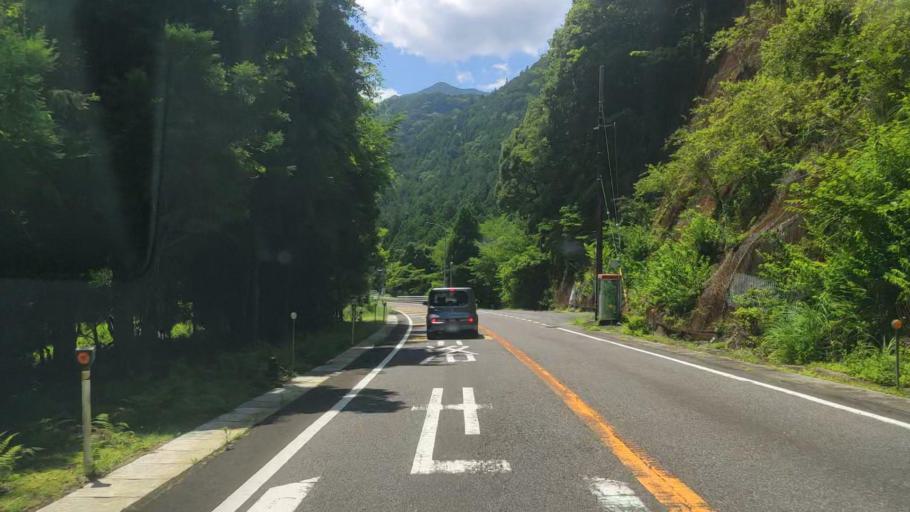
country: JP
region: Mie
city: Owase
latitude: 33.9921
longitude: 136.1193
